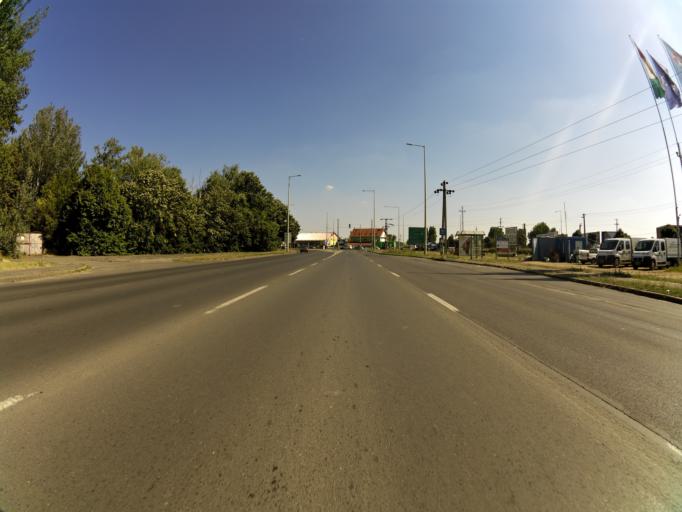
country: HU
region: Csongrad
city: Szeged
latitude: 46.2689
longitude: 20.1035
